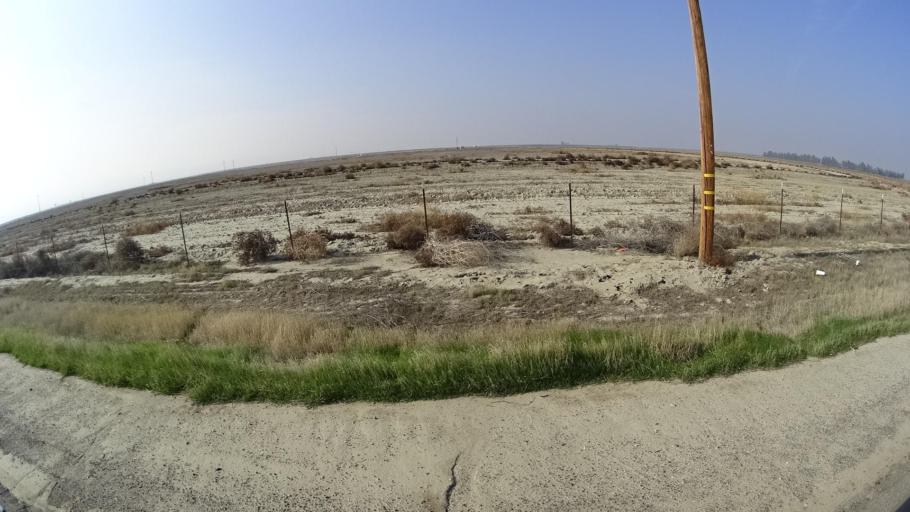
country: US
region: California
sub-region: Kern County
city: Buttonwillow
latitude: 35.3466
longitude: -119.3591
